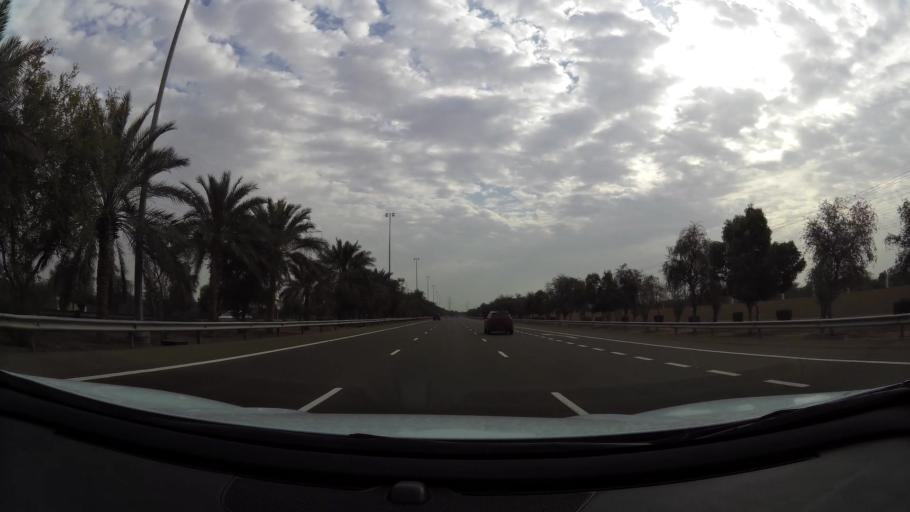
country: AE
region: Abu Dhabi
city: Al Ain
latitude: 24.2080
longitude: 55.4408
